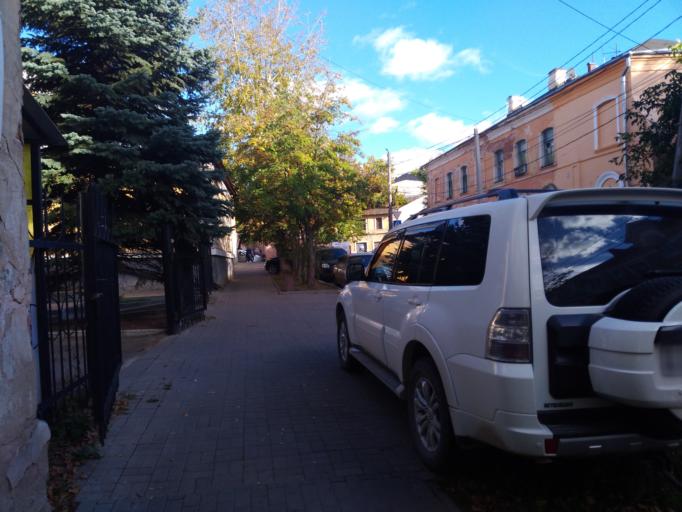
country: RU
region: Kaluga
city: Kaluga
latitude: 54.5099
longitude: 36.2532
